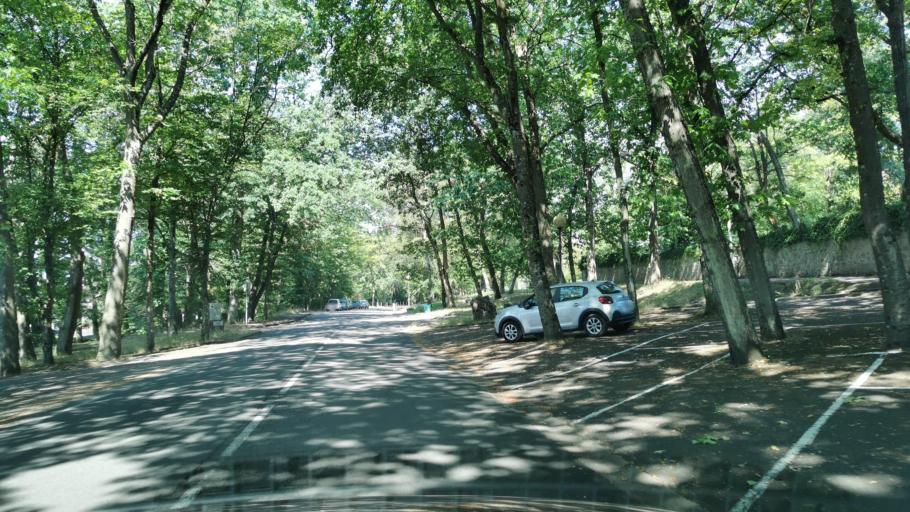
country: FR
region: Bourgogne
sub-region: Departement de Saone-et-Loire
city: Le Creusot
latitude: 46.8000
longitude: 4.4246
